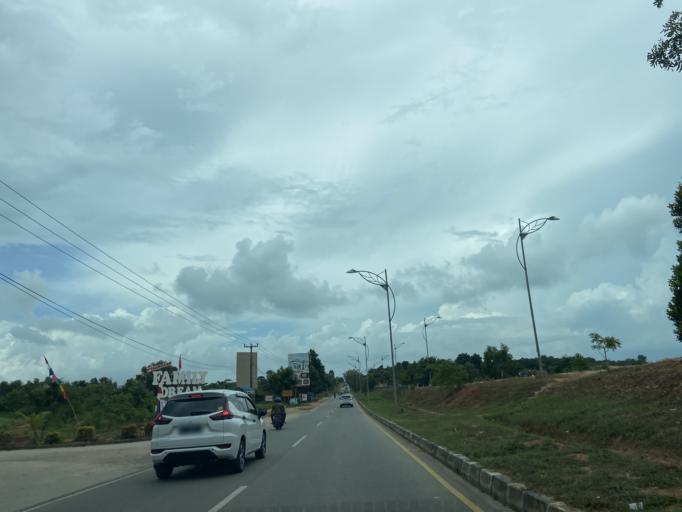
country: SG
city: Singapore
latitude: 1.1398
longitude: 104.1204
